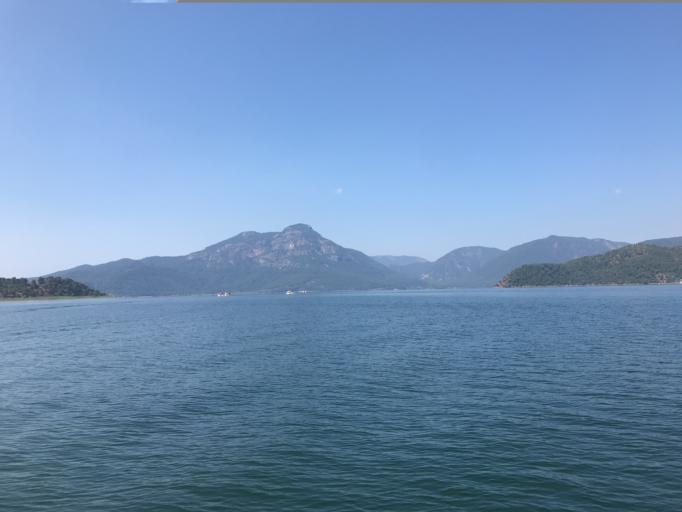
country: TR
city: Dalyan
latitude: 36.9082
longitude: 28.6512
